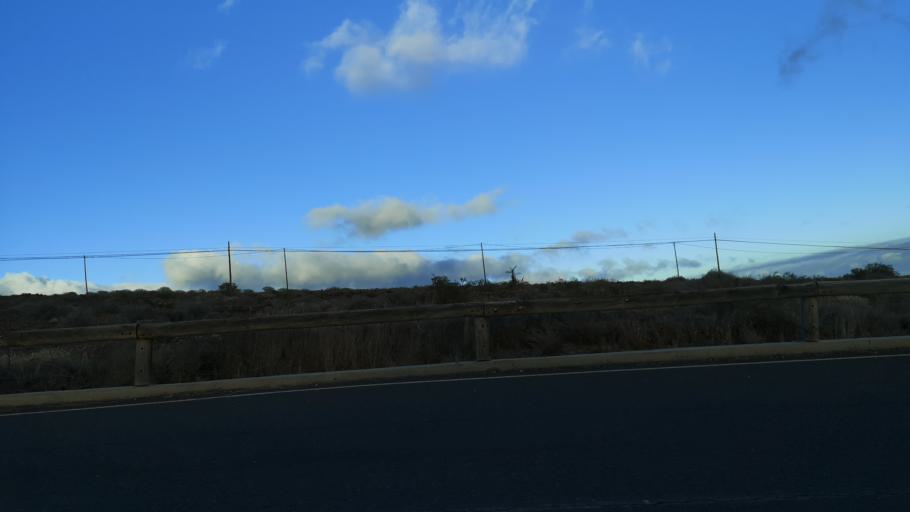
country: ES
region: Canary Islands
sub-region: Provincia de Santa Cruz de Tenerife
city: Alajero
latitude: 28.0366
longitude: -17.2196
